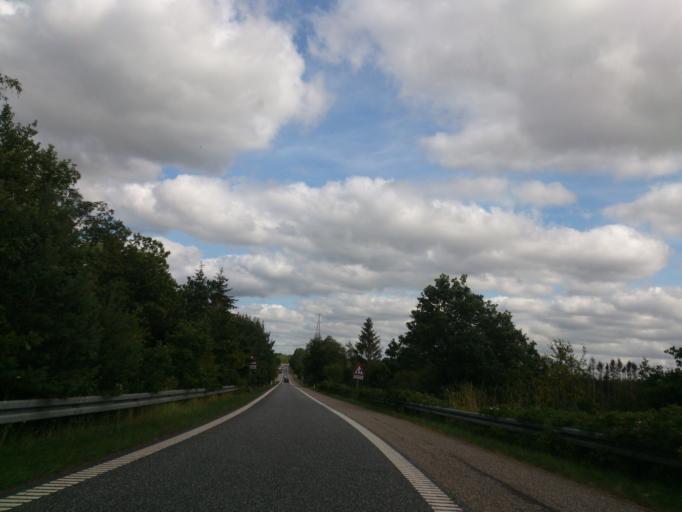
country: DK
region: South Denmark
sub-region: Aabenraa Kommune
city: Krusa
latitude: 54.8747
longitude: 9.3788
